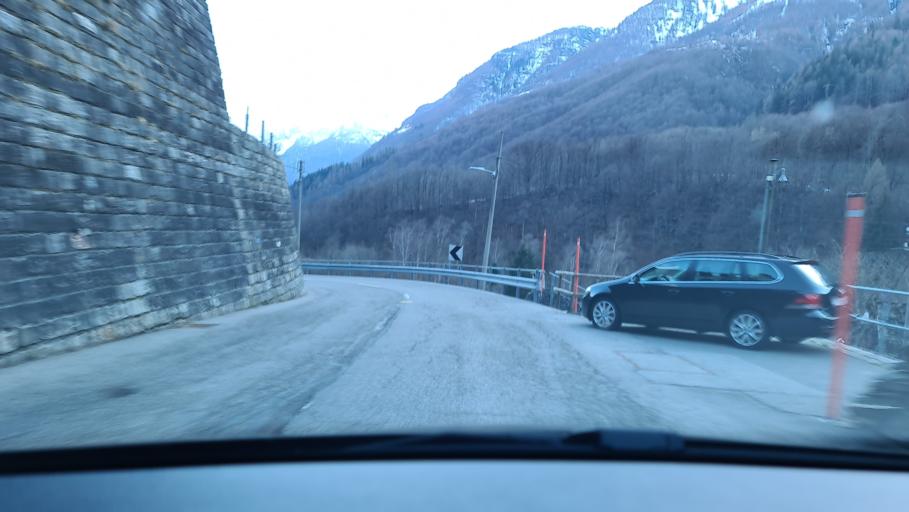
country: CH
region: Ticino
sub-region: Locarno District
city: Lavertezzo
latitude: 46.3368
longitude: 8.8055
